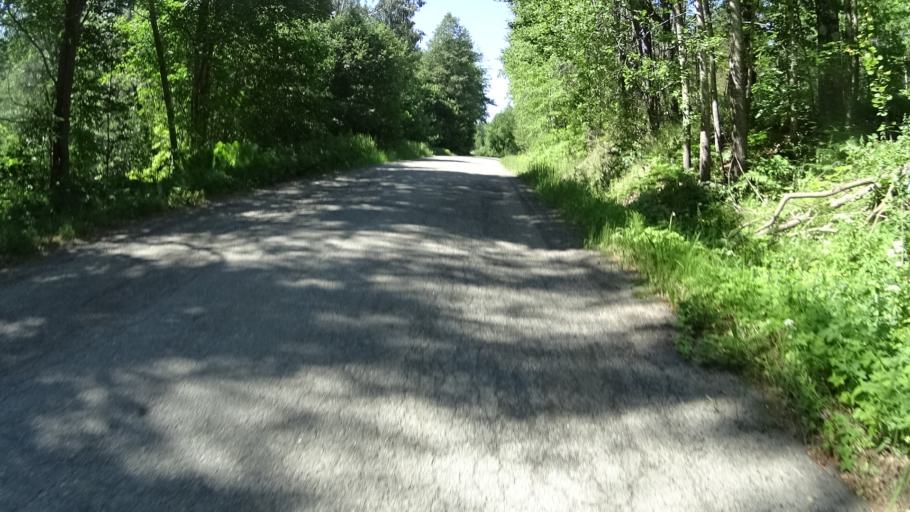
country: FI
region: Uusimaa
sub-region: Raaseporin
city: Pohja
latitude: 60.0946
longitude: 23.5760
